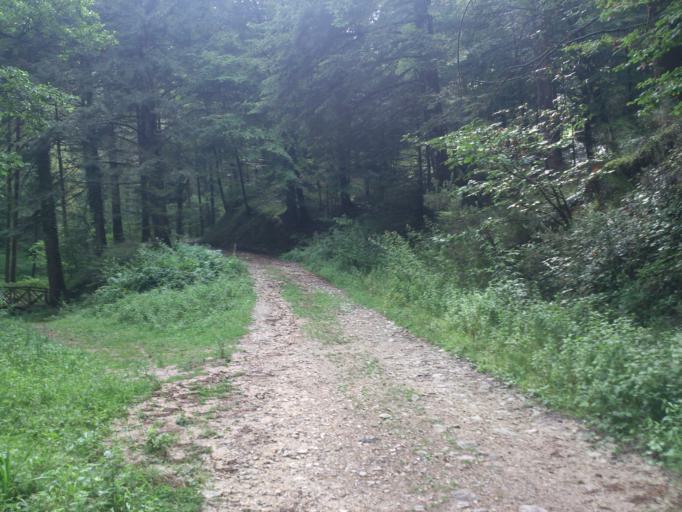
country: IT
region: Calabria
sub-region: Provincia di Vibo-Valentia
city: Serra San Bruno
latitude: 38.5485
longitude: 16.3091
